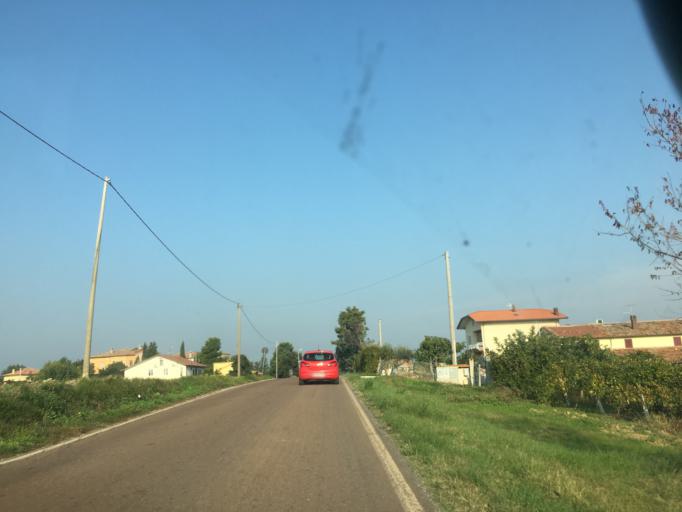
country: IT
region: Emilia-Romagna
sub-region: Provincia di Rimini
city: San Clemente
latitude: 43.9484
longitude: 12.6144
